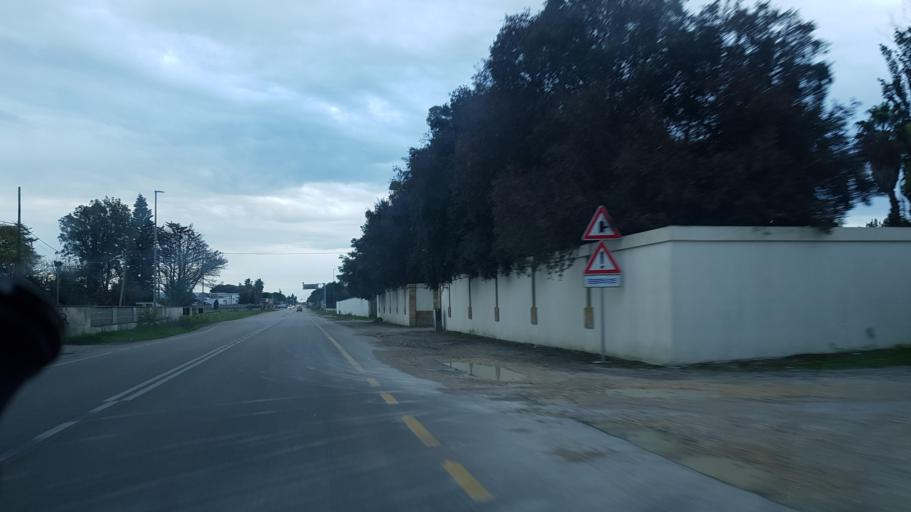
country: IT
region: Apulia
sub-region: Provincia di Lecce
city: Merine
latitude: 40.3415
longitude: 18.2155
